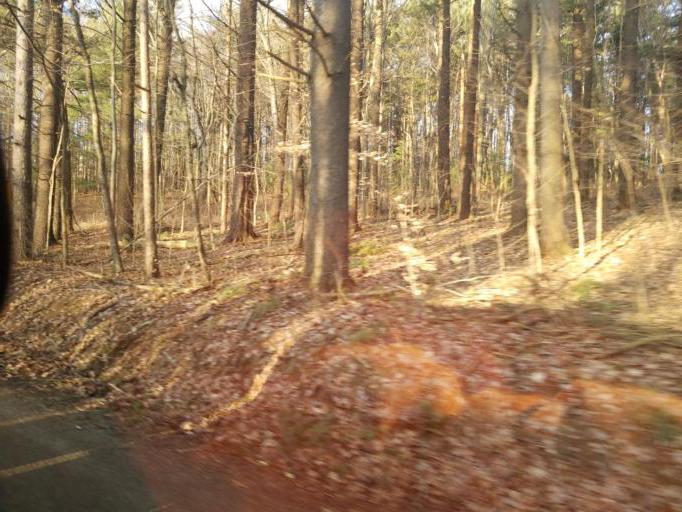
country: US
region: Ohio
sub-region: Sandusky County
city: Bellville
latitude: 40.5792
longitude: -82.4478
